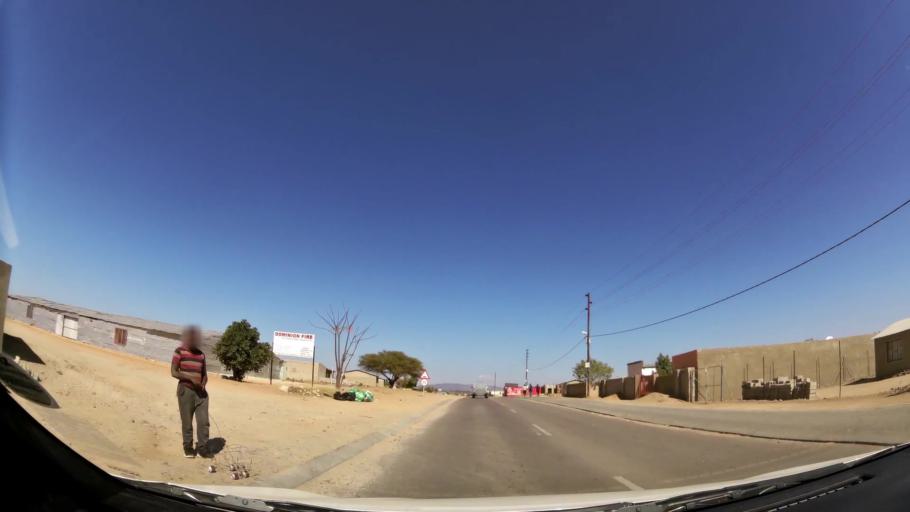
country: ZA
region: Limpopo
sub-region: Capricorn District Municipality
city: Polokwane
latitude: -23.8795
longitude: 29.4111
